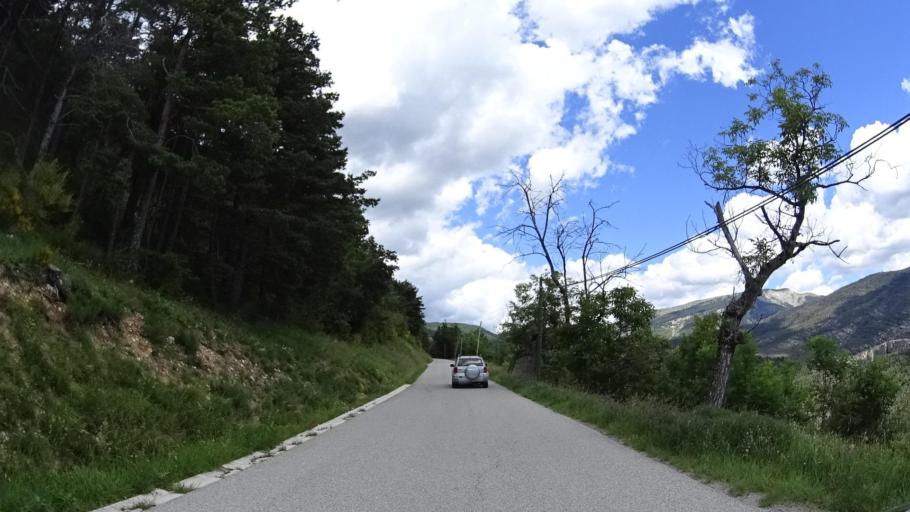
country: FR
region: Provence-Alpes-Cote d'Azur
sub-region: Departement des Alpes-de-Haute-Provence
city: Annot
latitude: 44.0263
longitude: 6.6169
